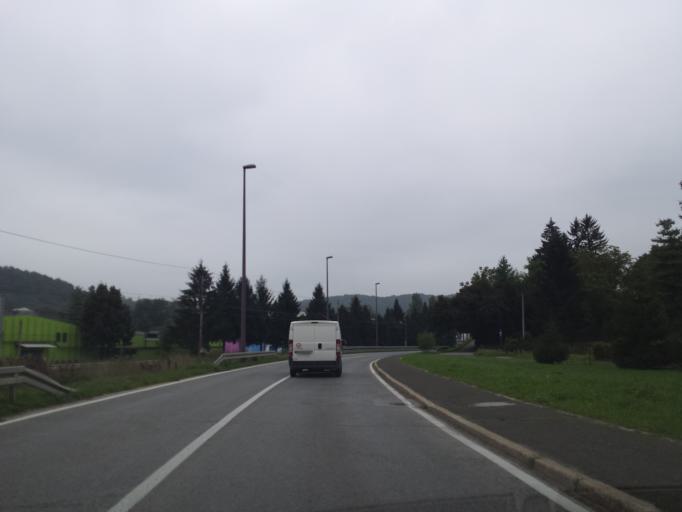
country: HR
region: Karlovacka
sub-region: Grad Karlovac
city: Karlovac
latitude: 45.4645
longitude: 15.5302
